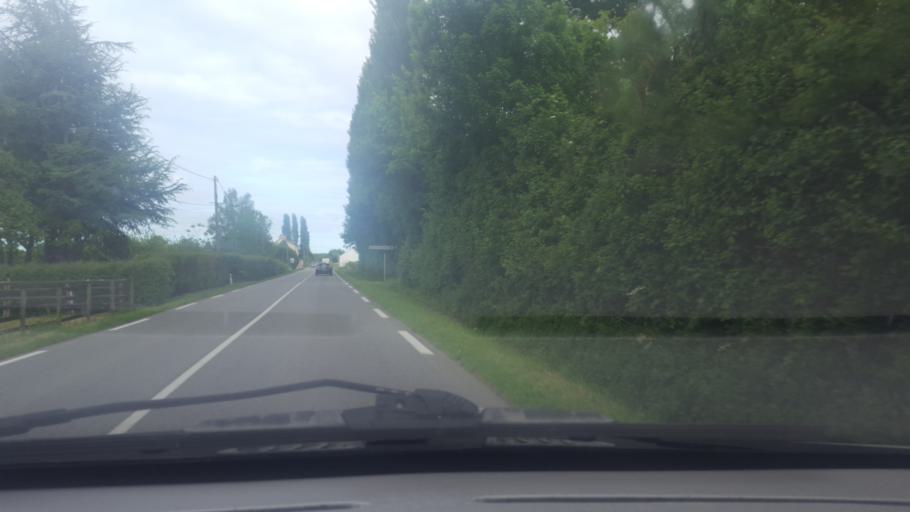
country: FR
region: Pays de la Loire
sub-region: Departement de la Loire-Atlantique
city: Machecoul
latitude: 47.0235
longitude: -1.8749
